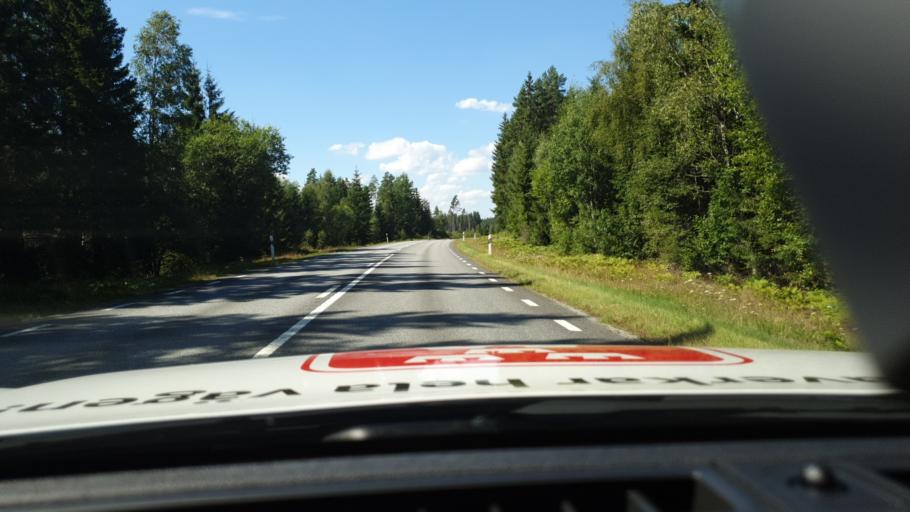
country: SE
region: Joenkoeping
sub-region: Savsjo Kommun
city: Vrigstad
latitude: 57.3700
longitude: 14.4209
